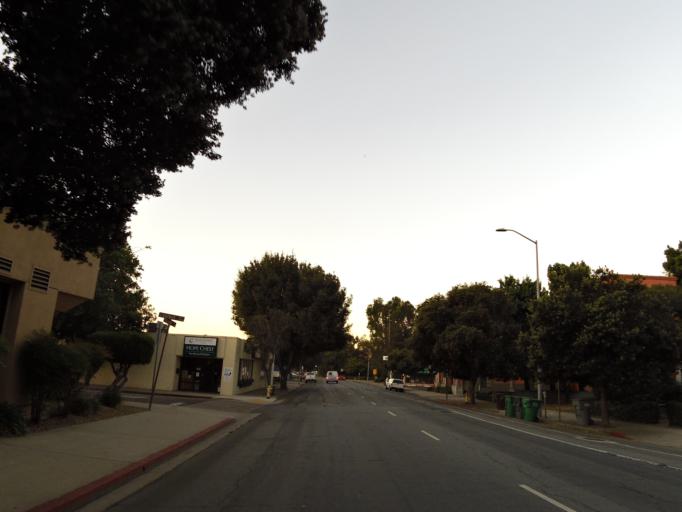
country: US
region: California
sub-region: San Luis Obispo County
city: San Luis Obispo
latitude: 35.2765
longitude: -120.6683
